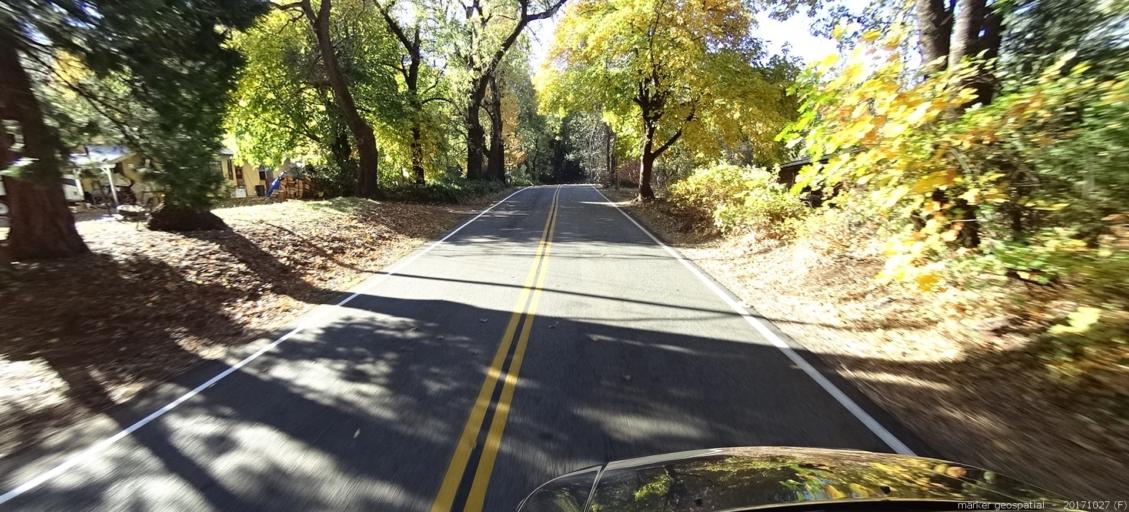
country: US
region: California
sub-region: Shasta County
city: Burney
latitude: 40.8929
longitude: -121.9057
